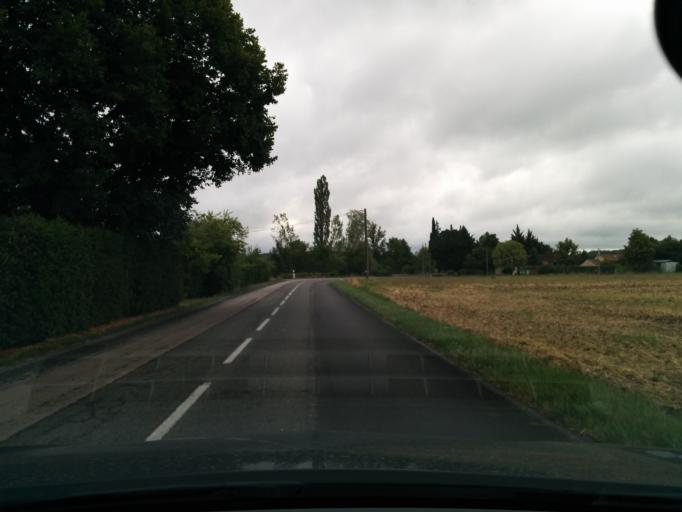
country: FR
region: Midi-Pyrenees
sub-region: Departement du Lot
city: Montcuq
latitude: 44.3541
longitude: 1.2237
